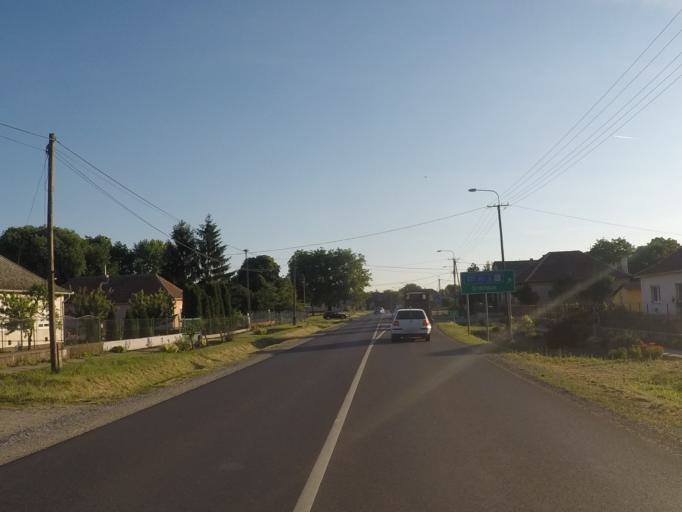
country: HU
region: Heves
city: Erdotelek
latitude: 47.6571
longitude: 20.3442
